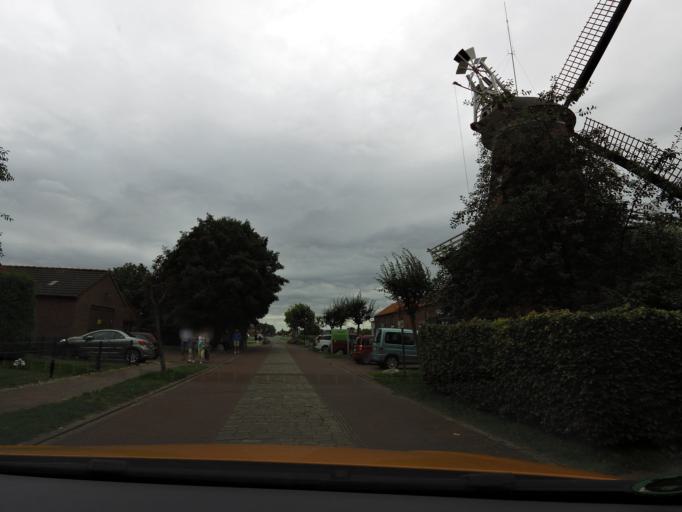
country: DE
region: Lower Saxony
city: Wirdum
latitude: 53.4975
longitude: 7.1007
